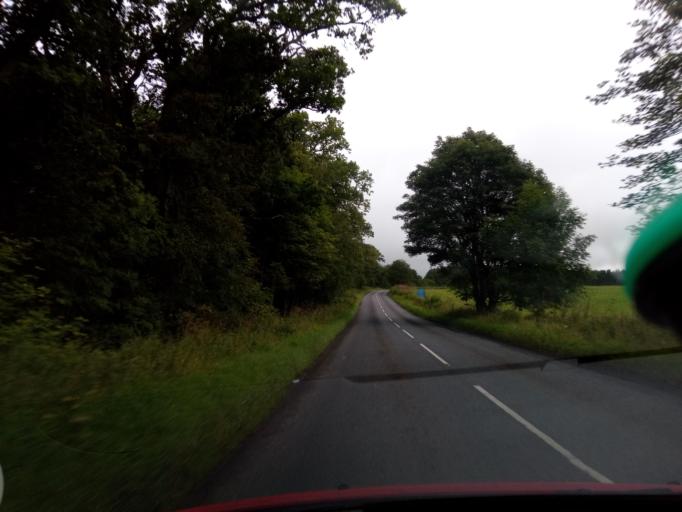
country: GB
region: Scotland
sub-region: The Scottish Borders
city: Saint Boswells
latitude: 55.6538
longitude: -2.5474
